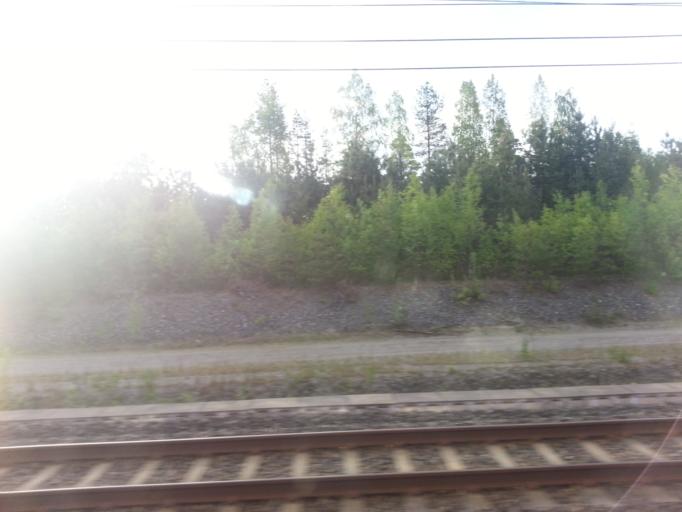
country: NO
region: Akershus
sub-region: Nannestad
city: Teigebyen
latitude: 60.2047
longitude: 11.1034
